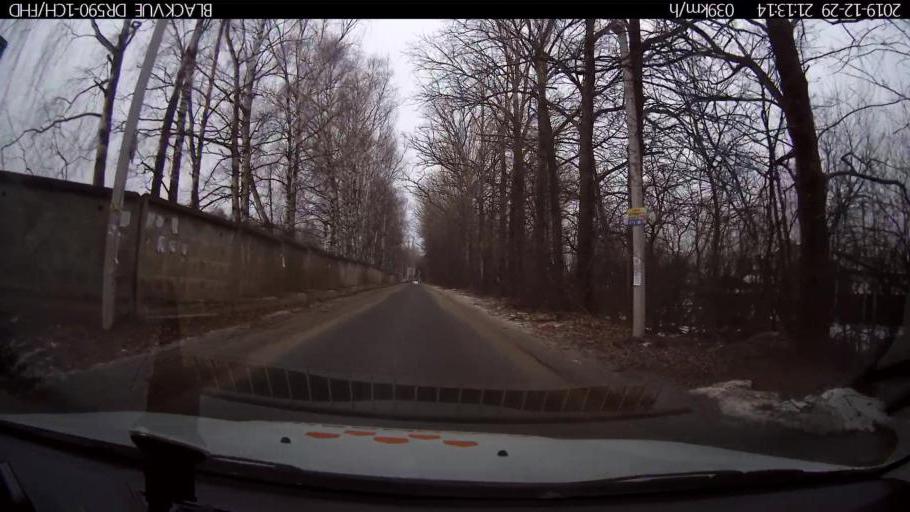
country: RU
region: Nizjnij Novgorod
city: Afonino
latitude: 56.2201
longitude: 44.0374
